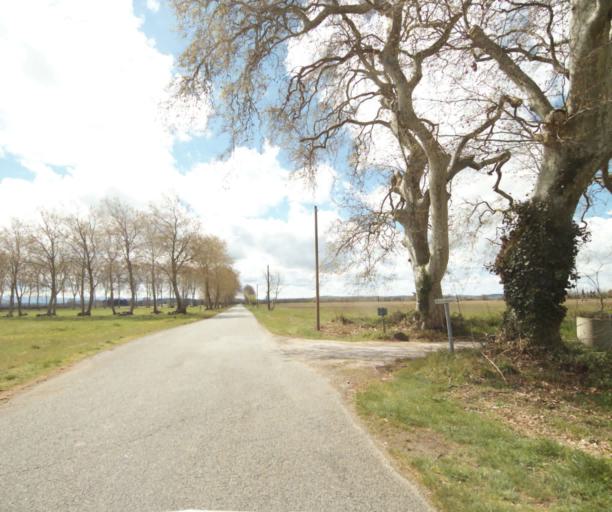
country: FR
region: Midi-Pyrenees
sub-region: Departement de l'Ariege
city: Saverdun
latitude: 43.2582
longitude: 1.6039
